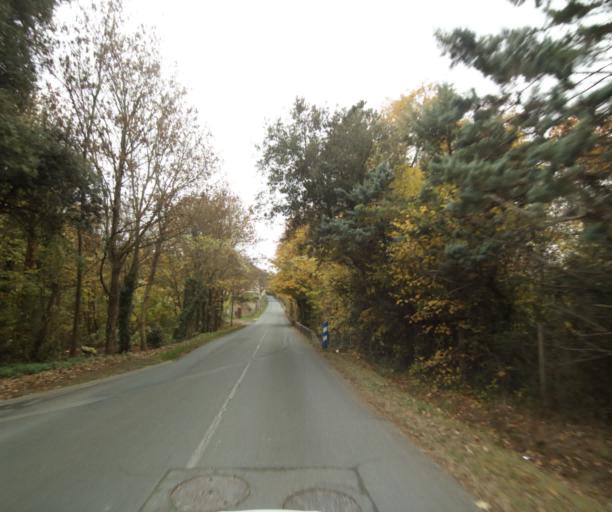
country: FR
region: Poitou-Charentes
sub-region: Departement de la Charente-Maritime
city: Les Gonds
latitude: 45.7247
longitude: -0.6347
